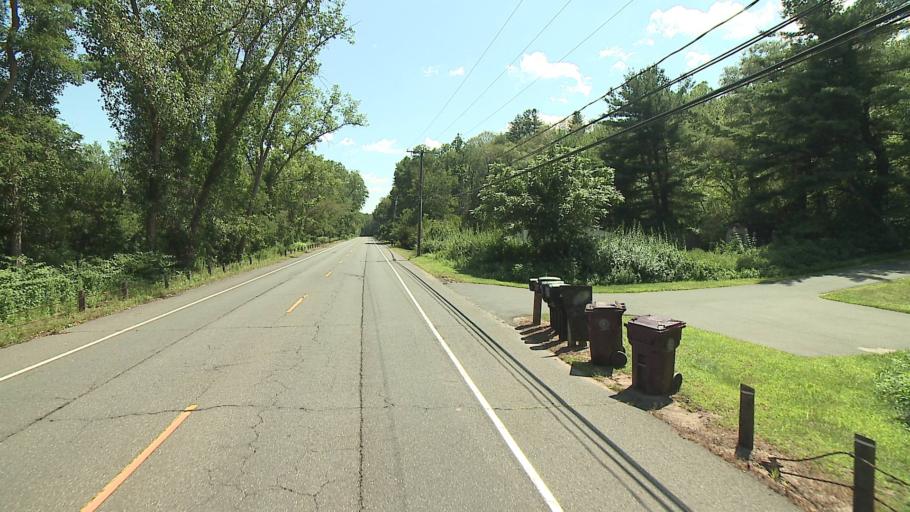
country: US
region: Connecticut
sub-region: Hartford County
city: Collinsville
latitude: 41.7716
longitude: -72.9044
